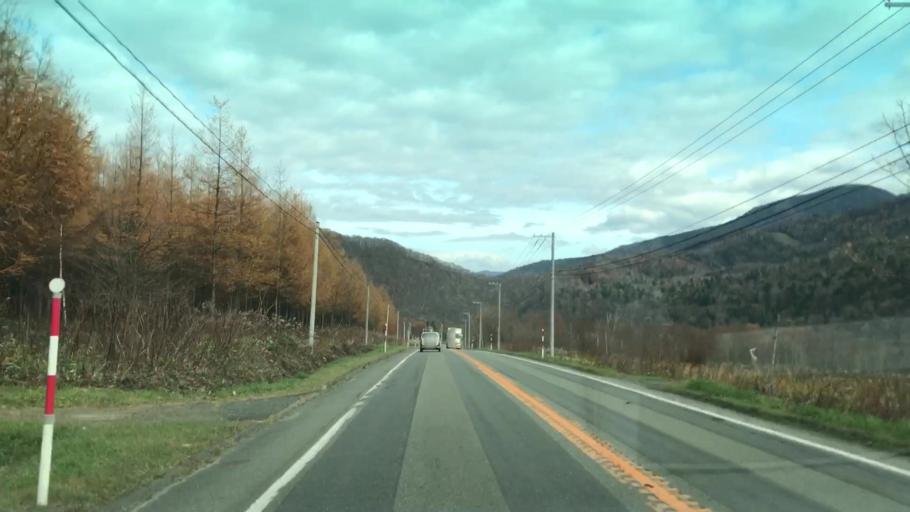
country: JP
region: Hokkaido
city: Shizunai-furukawacho
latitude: 42.7812
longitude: 142.3919
